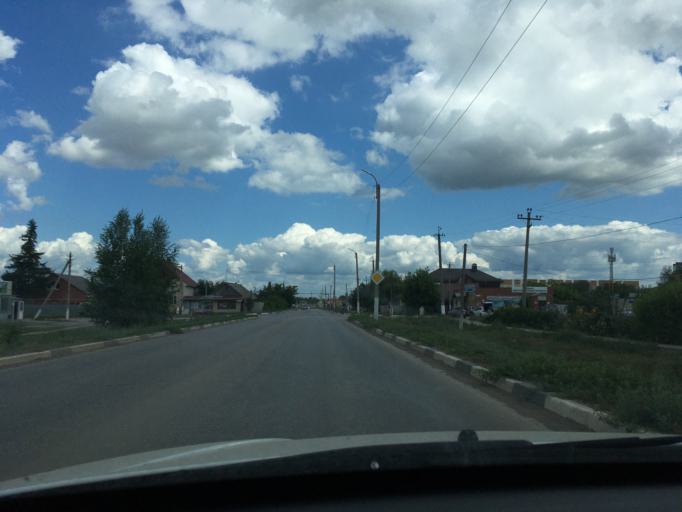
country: RU
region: Samara
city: Bezenchuk
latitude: 52.9885
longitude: 49.4352
